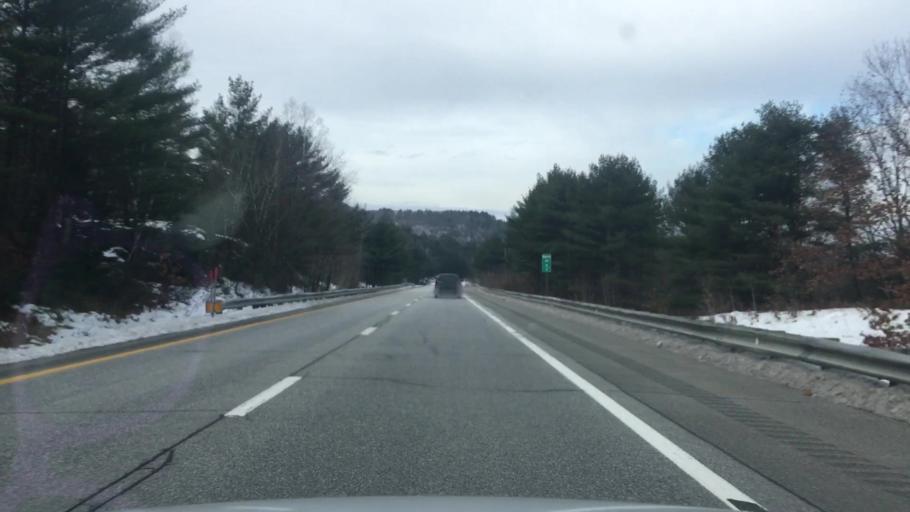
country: US
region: New Hampshire
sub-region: Merrimack County
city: Henniker
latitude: 43.2781
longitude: -71.8196
